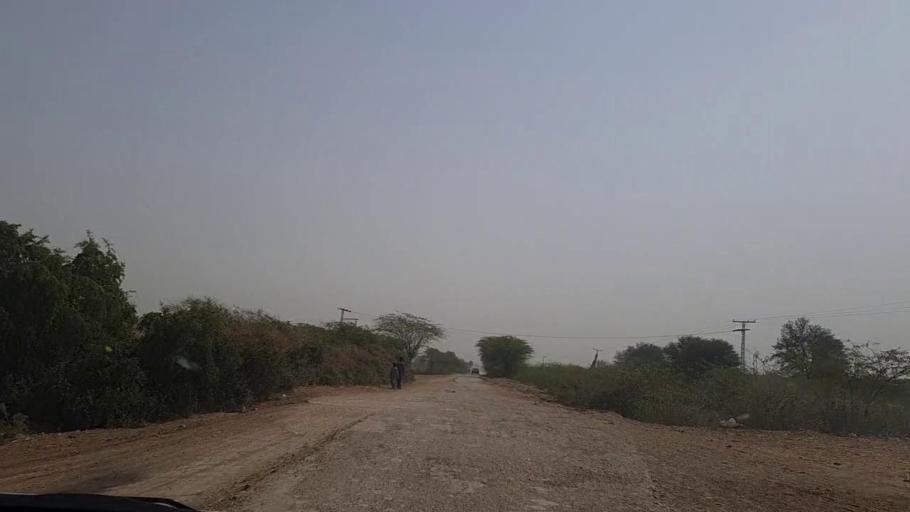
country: PK
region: Sindh
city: Pithoro
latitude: 25.4816
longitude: 69.2196
